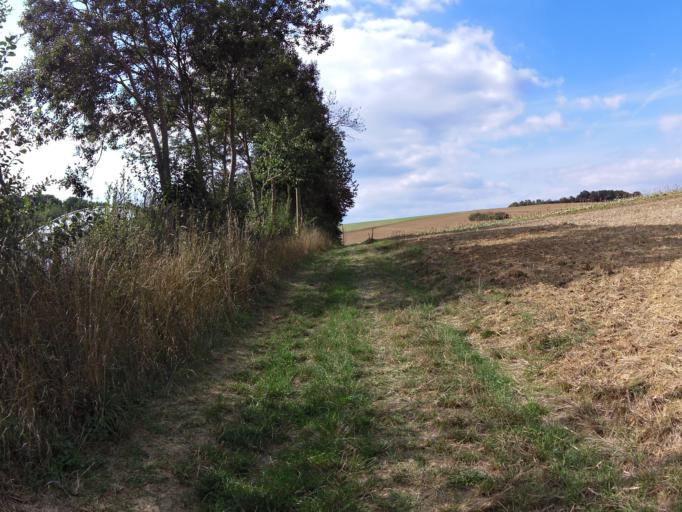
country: DE
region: Bavaria
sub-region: Regierungsbezirk Unterfranken
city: Hettstadt
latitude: 49.7896
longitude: 9.8035
